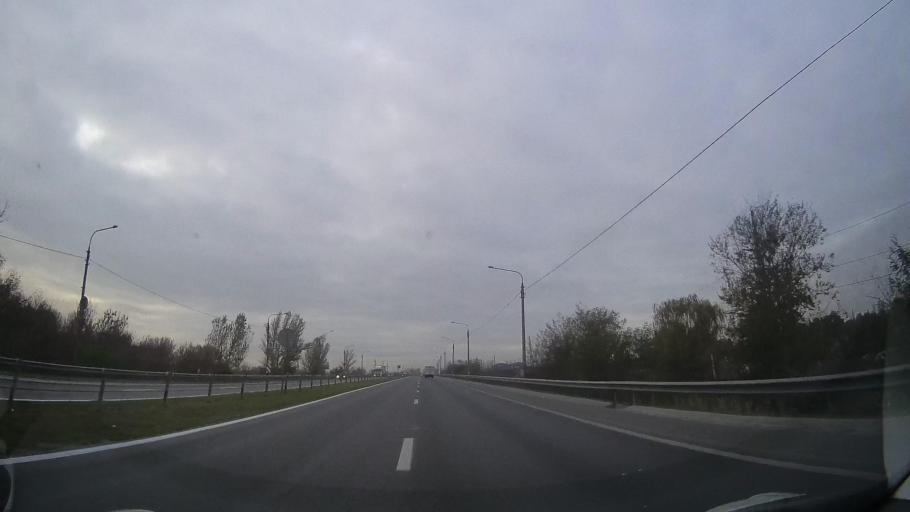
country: RU
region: Rostov
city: Bataysk
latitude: 47.1228
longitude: 39.7724
